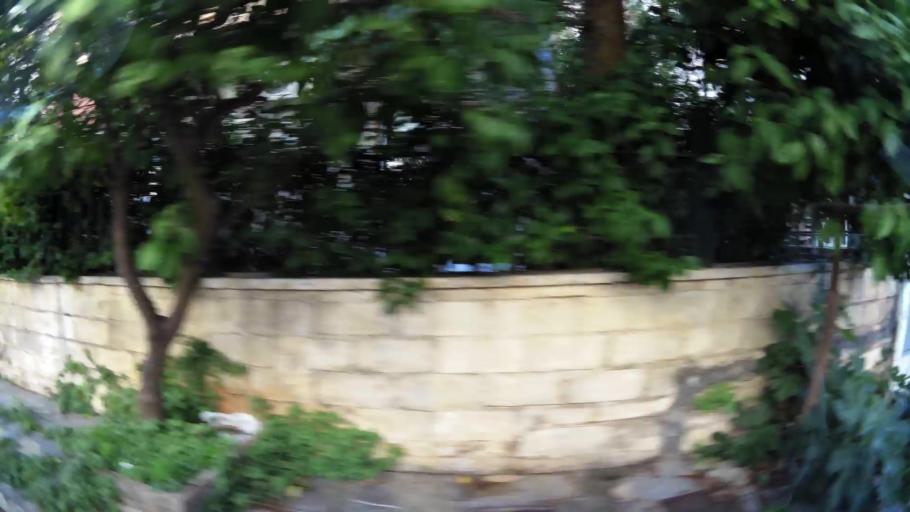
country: GR
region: Attica
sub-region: Nomarchia Athinas
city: Glyfada
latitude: 37.8736
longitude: 23.7717
